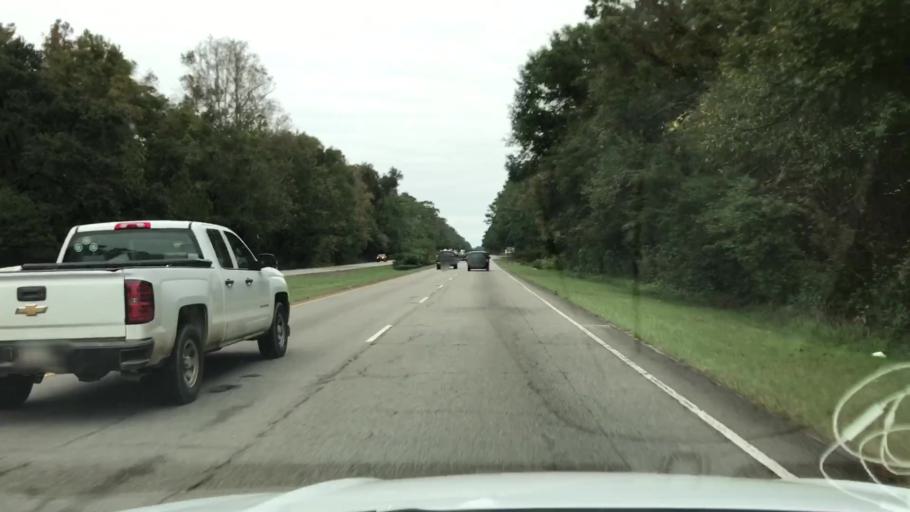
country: US
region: South Carolina
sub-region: Georgetown County
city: Murrells Inlet
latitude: 33.5113
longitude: -79.0749
